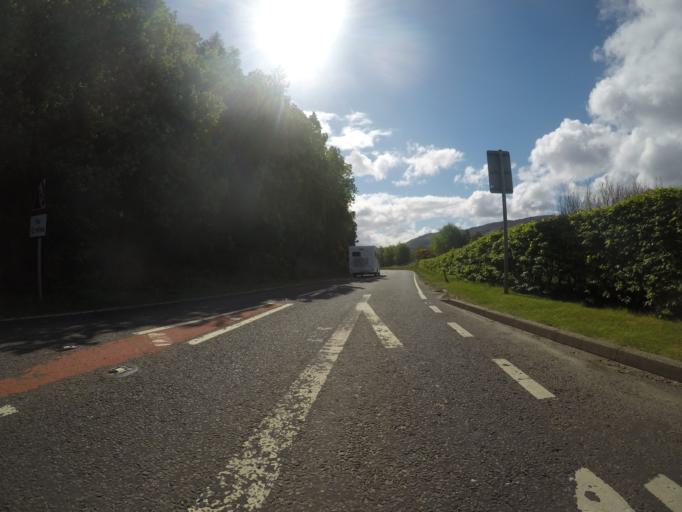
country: GB
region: Scotland
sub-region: Highland
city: Fort William
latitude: 57.2732
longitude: -5.5125
